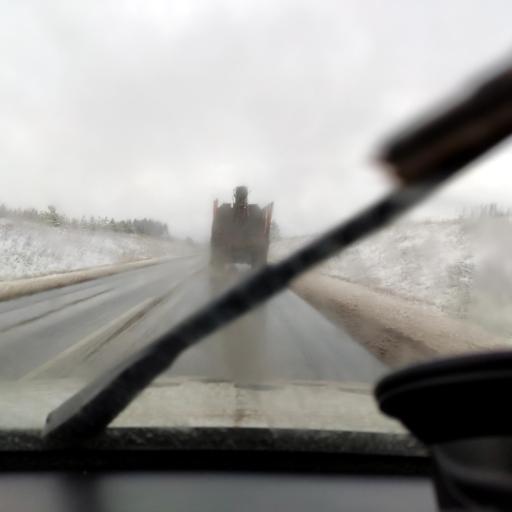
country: RU
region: Perm
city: Nytva
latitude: 57.9668
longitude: 55.3639
